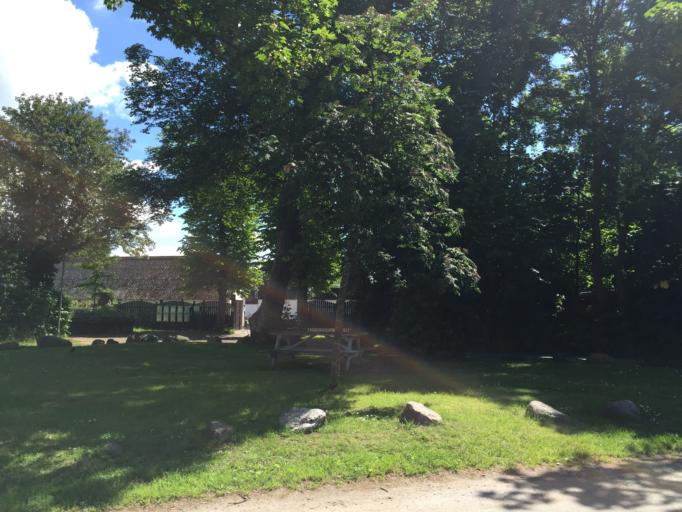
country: DK
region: Capital Region
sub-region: Frederikssund Kommune
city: Skibby
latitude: 55.7180
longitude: 11.9771
